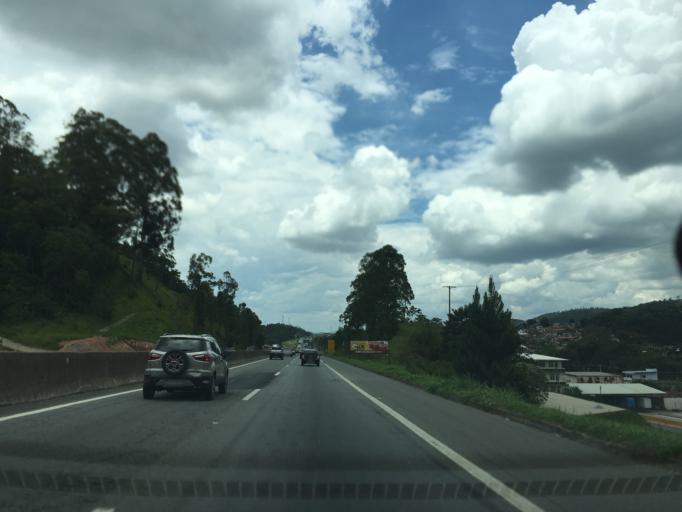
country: BR
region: Sao Paulo
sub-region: Mairipora
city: Mairipora
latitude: -23.2232
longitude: -46.5968
